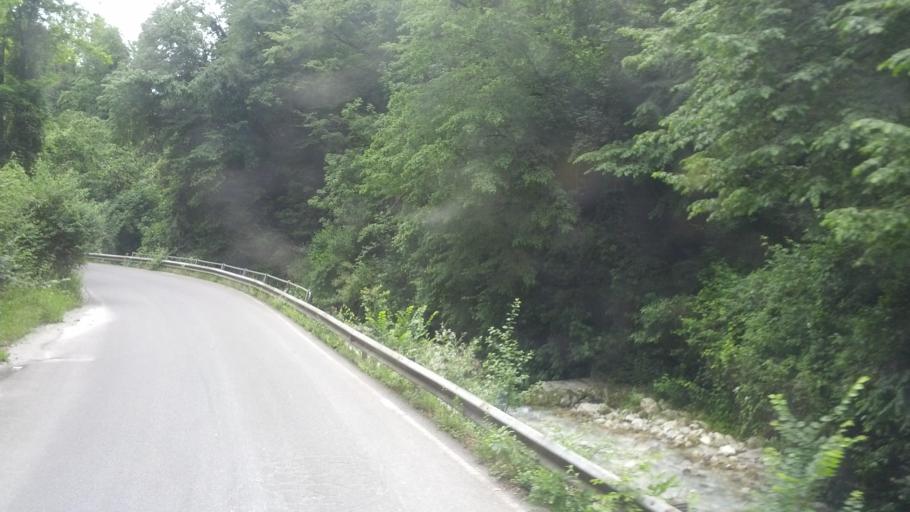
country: IT
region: Tuscany
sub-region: Provincia di Massa-Carrara
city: Carrara
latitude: 44.0864
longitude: 10.1033
